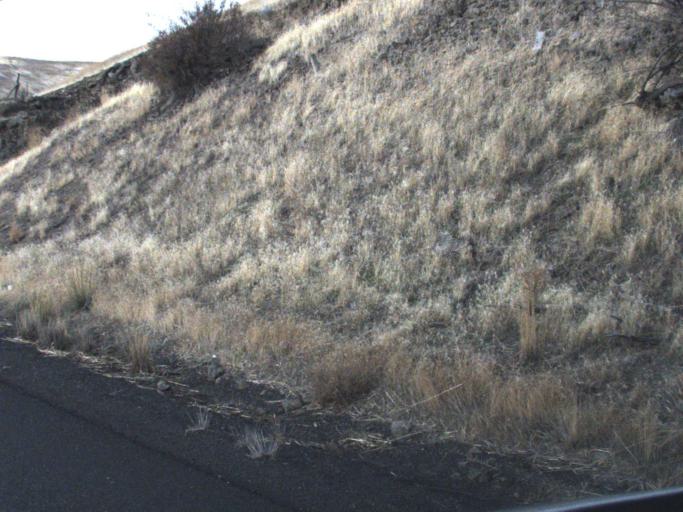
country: US
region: Washington
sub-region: Garfield County
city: Pomeroy
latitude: 46.4705
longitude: -117.5196
